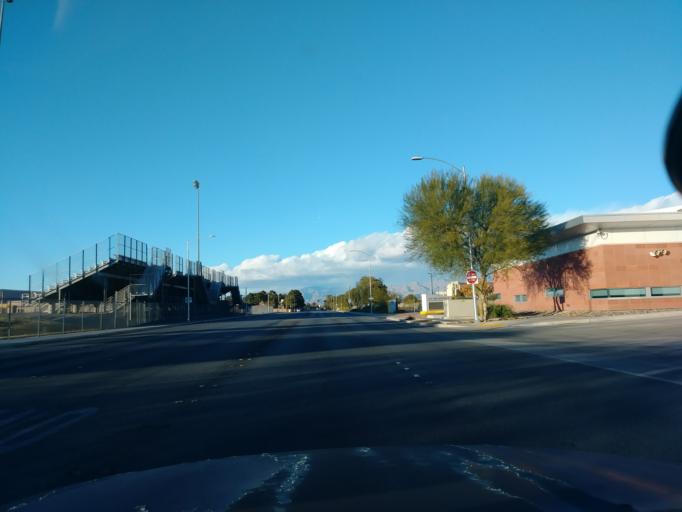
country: US
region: Nevada
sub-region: Clark County
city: Spring Valley
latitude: 36.1520
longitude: -115.2343
